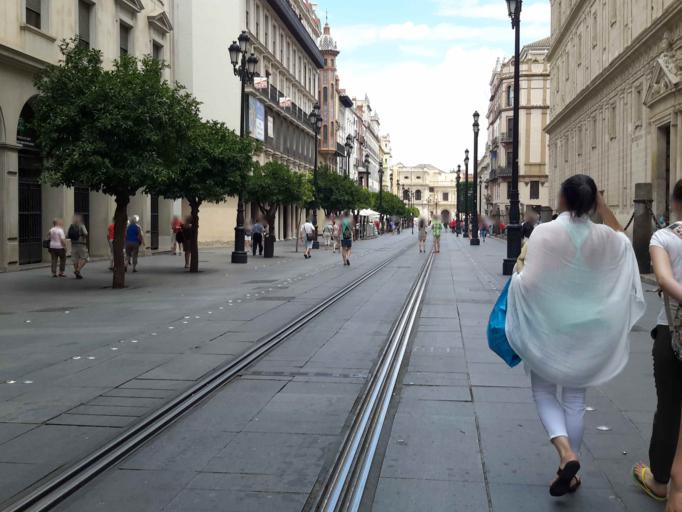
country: ES
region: Andalusia
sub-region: Provincia de Sevilla
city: Sevilla
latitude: 37.3857
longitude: -5.9940
